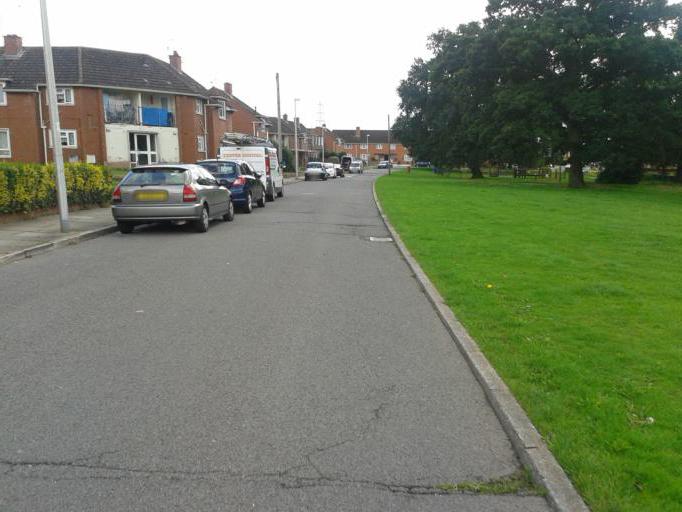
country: GB
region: England
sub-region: Devon
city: Exminster
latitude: 50.6961
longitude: -3.4887
